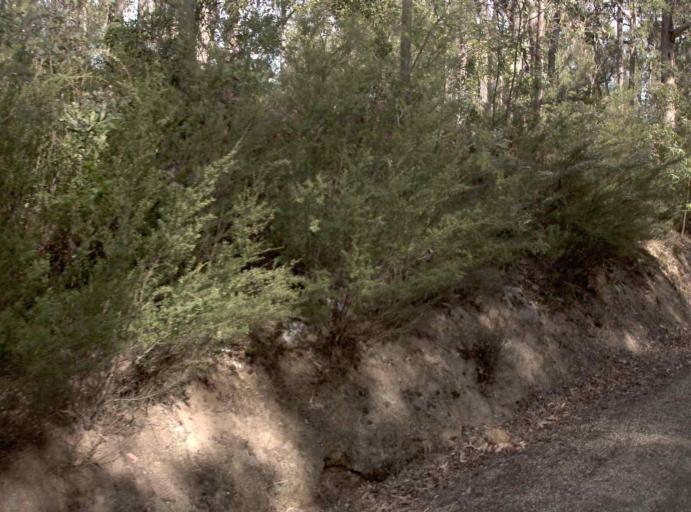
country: AU
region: Victoria
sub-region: East Gippsland
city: Lakes Entrance
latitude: -37.5476
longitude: 148.1481
